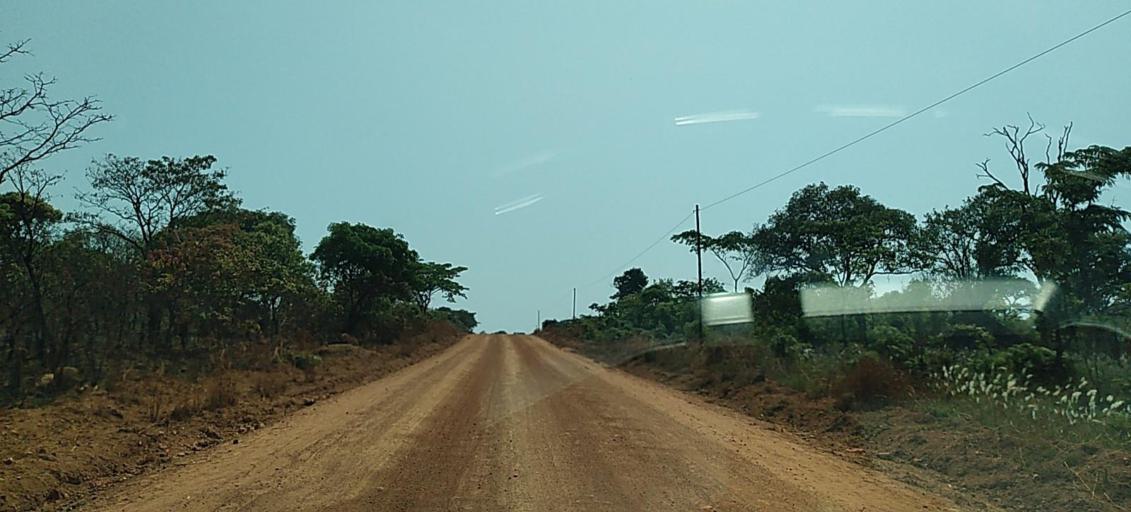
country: ZM
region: North-Western
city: Kansanshi
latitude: -11.9983
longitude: 26.5943
